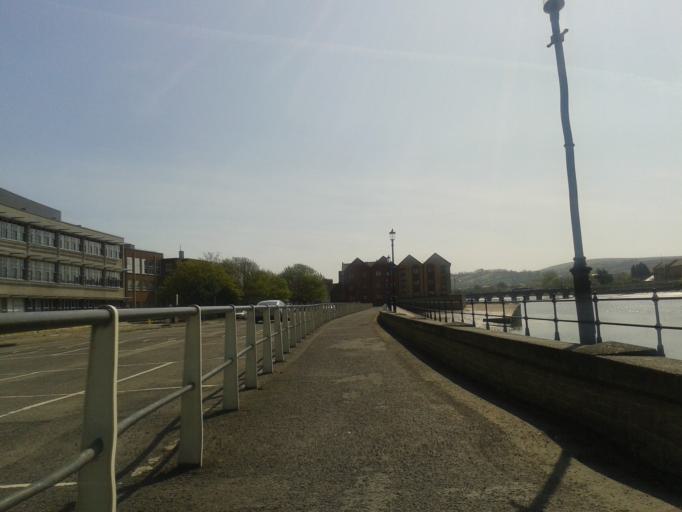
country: GB
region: England
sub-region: Devon
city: Barnstaple
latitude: 51.0810
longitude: -4.0661
